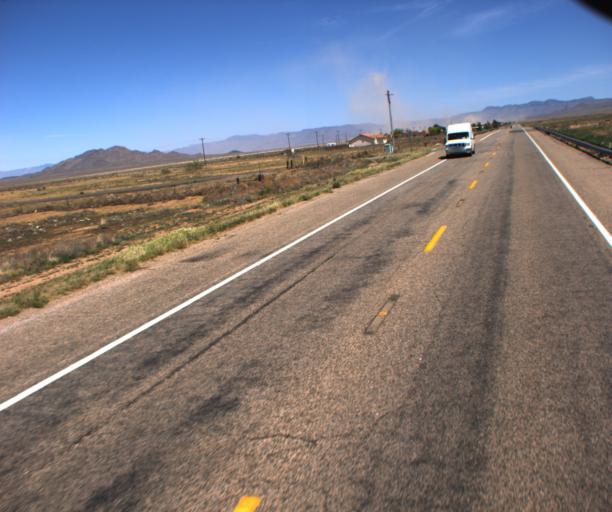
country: US
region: Arizona
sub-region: Mohave County
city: New Kingman-Butler
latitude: 35.2942
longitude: -113.9371
